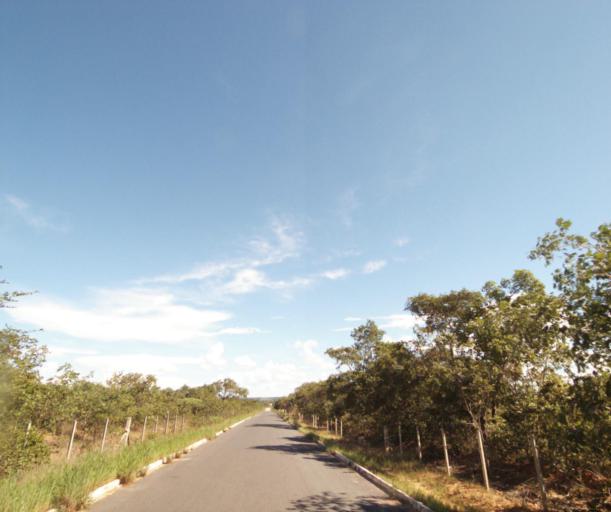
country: BR
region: Bahia
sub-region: Correntina
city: Correntina
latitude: -13.3116
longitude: -44.6408
